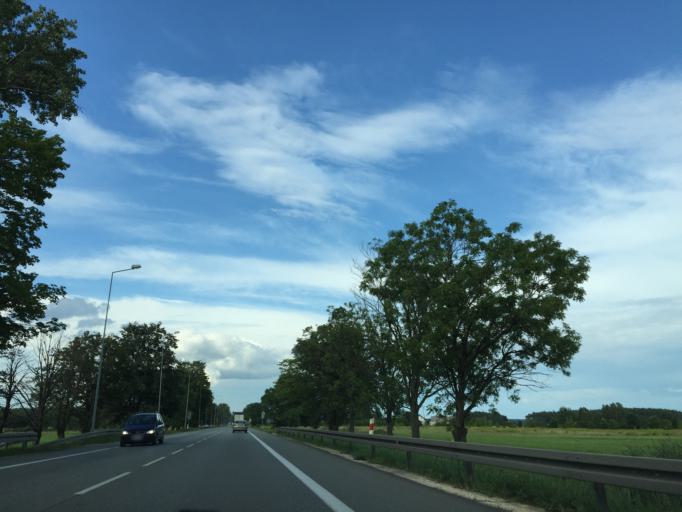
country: PL
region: Masovian Voivodeship
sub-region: Powiat otwocki
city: Karczew
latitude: 52.0194
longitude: 21.2951
